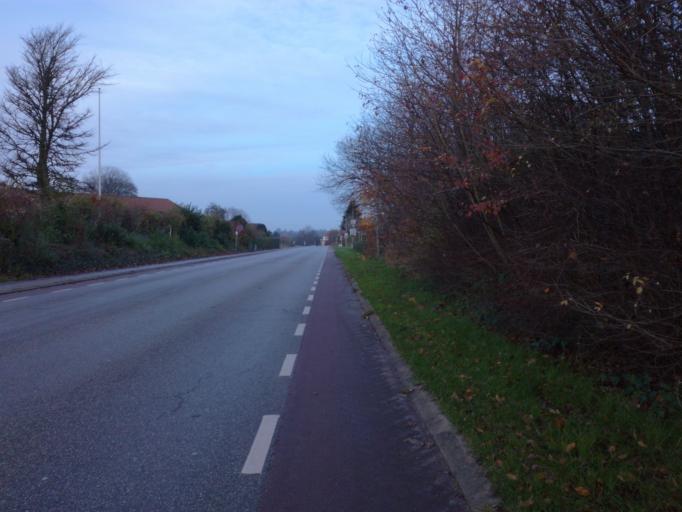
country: DK
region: South Denmark
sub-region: Vejle Kommune
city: Borkop
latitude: 55.6386
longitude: 9.6530
